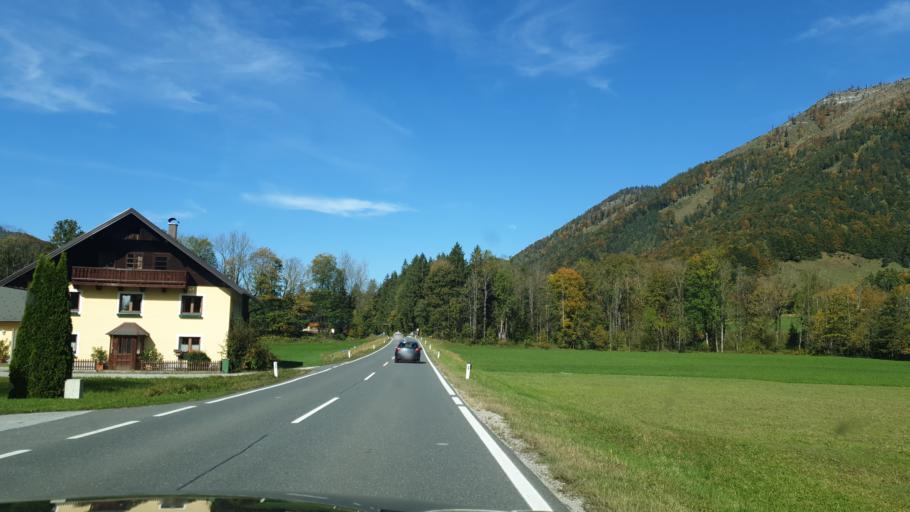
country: AT
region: Salzburg
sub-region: Politischer Bezirk Salzburg-Umgebung
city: Hintersee
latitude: 47.7335
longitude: 13.2655
